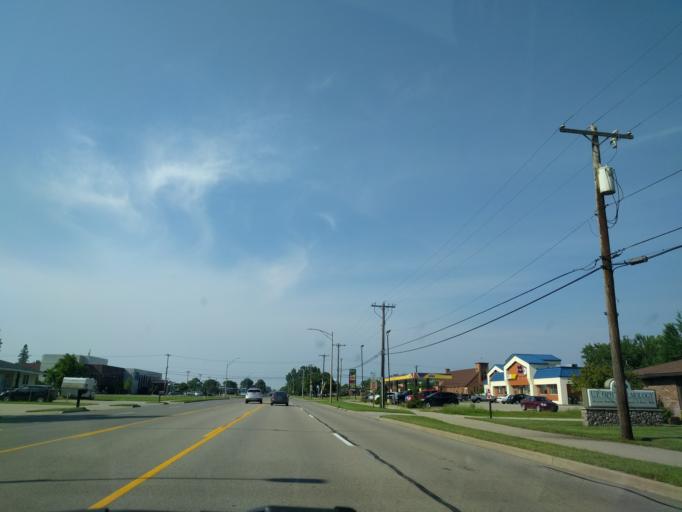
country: US
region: Michigan
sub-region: Delta County
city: Escanaba
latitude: 45.7341
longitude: -87.0799
